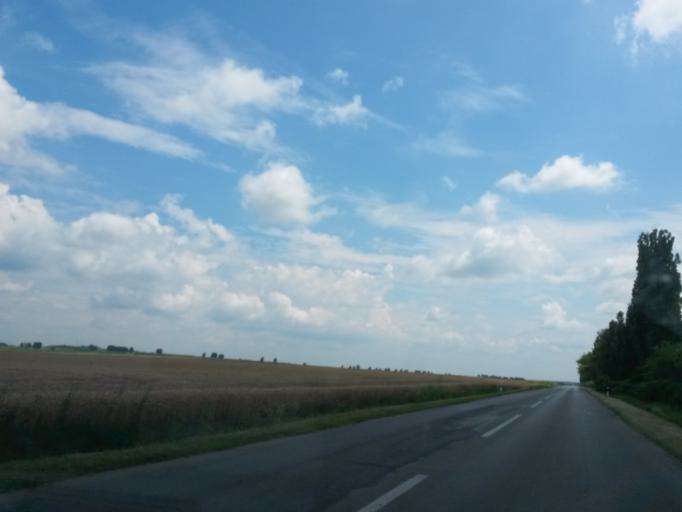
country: HR
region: Osjecko-Baranjska
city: Dalj
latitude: 45.5138
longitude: 18.9254
